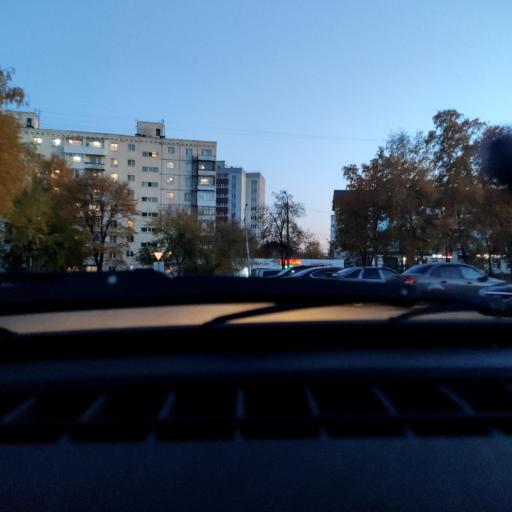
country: RU
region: Bashkortostan
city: Ufa
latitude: 54.8049
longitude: 56.1224
